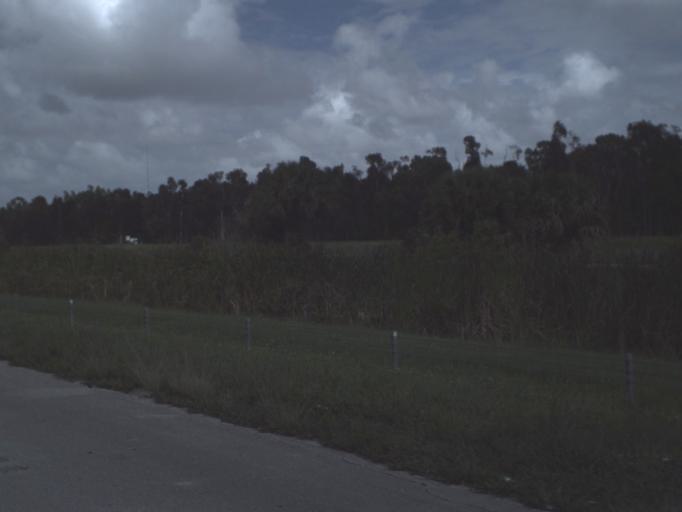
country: US
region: Florida
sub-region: Palm Beach County
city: Schall Circle
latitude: 26.7301
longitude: -80.1352
